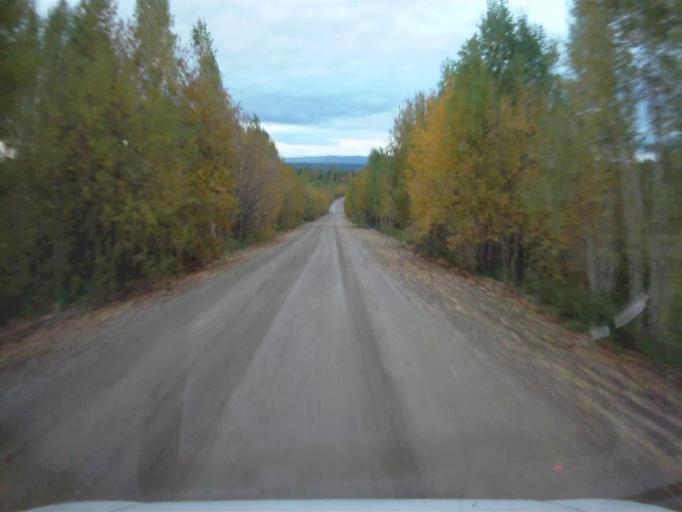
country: RU
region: Sverdlovsk
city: Mikhaylovsk
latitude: 56.2040
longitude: 59.2025
